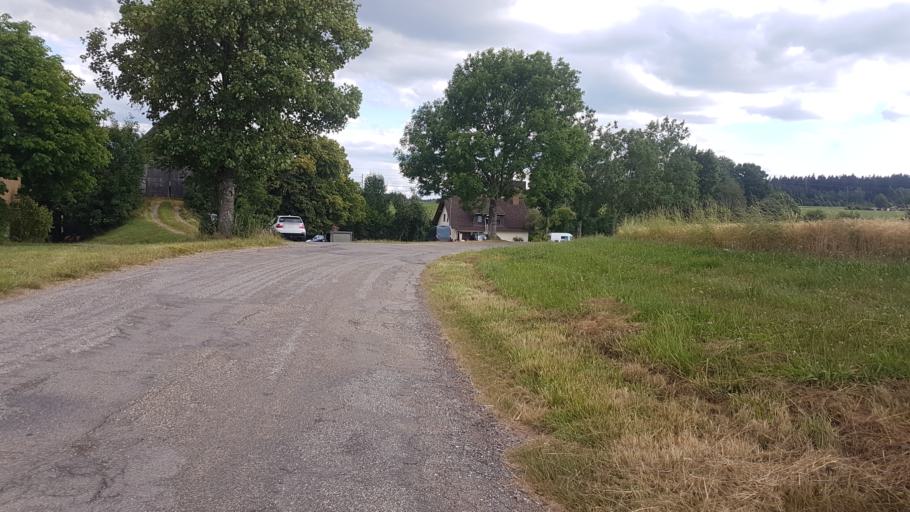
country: DE
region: Baden-Wuerttemberg
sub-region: Freiburg Region
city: Unterkirnach
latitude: 48.0304
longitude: 8.4086
